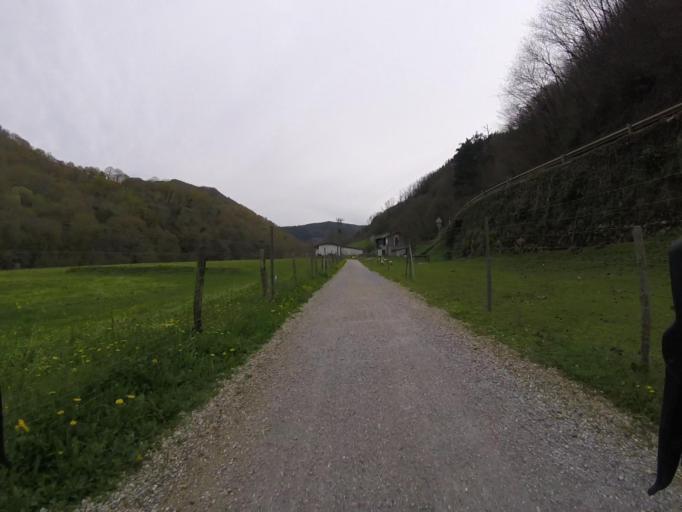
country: ES
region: Navarre
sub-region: Provincia de Navarra
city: Bera
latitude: 43.3090
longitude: -1.7361
